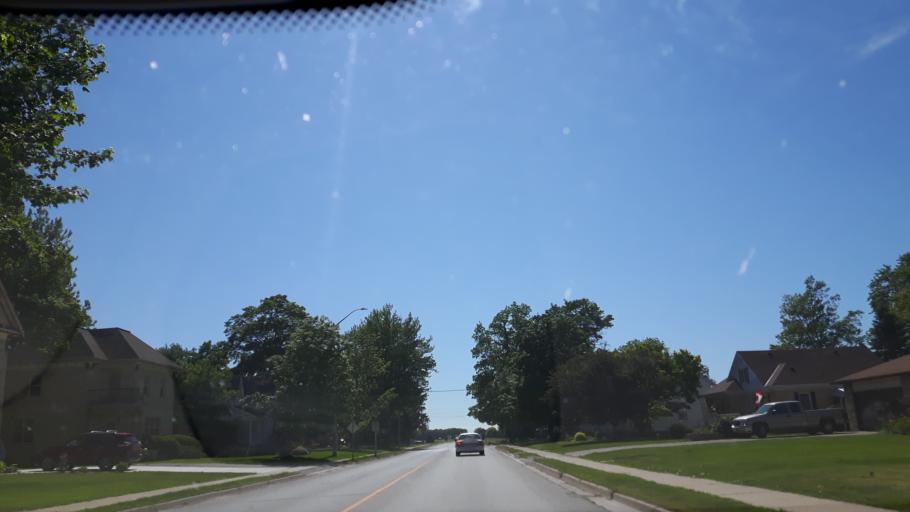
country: CA
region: Ontario
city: Bluewater
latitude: 43.4335
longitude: -81.5085
